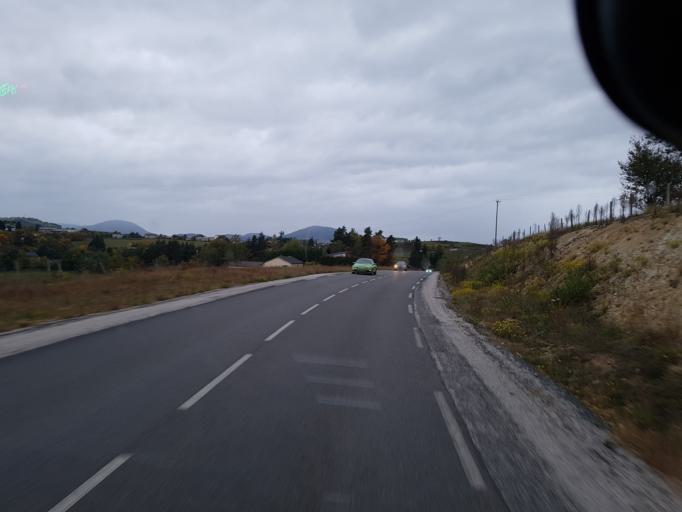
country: FR
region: Auvergne
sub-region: Departement de la Haute-Loire
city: Yssingeaux
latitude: 45.1611
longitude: 4.1450
